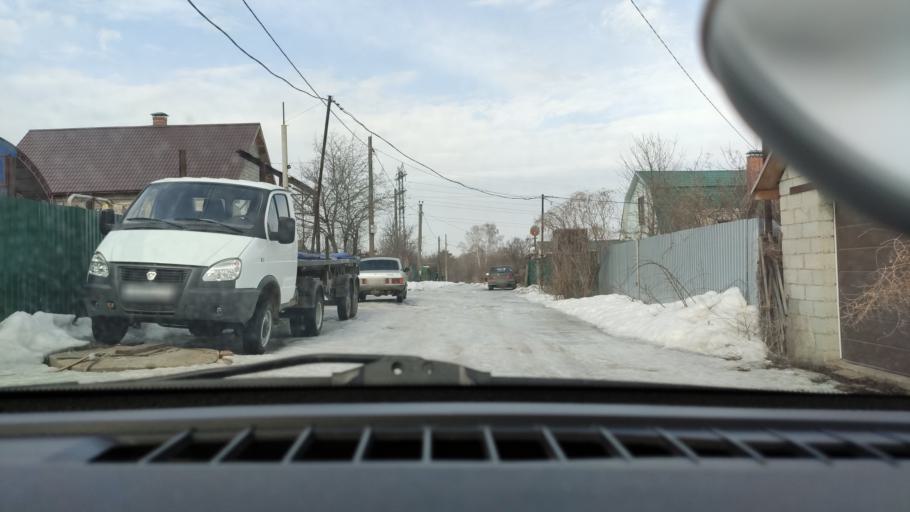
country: RU
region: Samara
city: Petra-Dubrava
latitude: 53.2654
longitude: 50.3059
